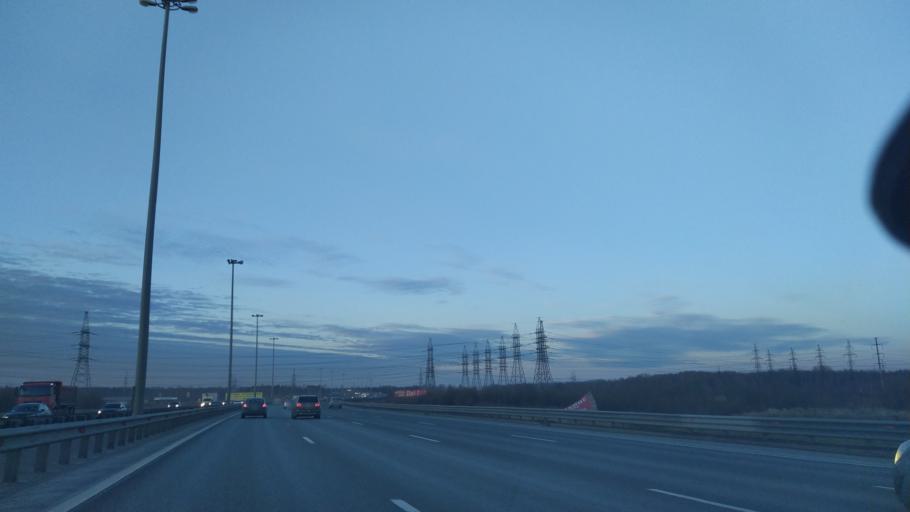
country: RU
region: St.-Petersburg
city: Krasnogvargeisky
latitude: 59.9211
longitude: 30.5273
